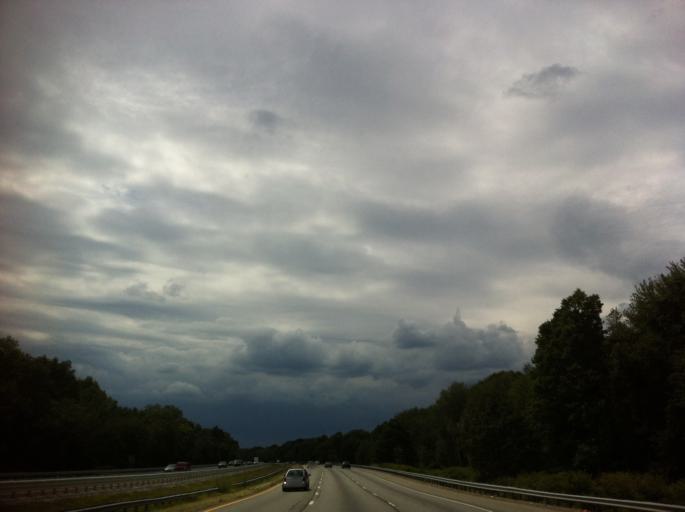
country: US
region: New Jersey
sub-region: Passaic County
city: Singac
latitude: 40.8966
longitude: -74.2534
